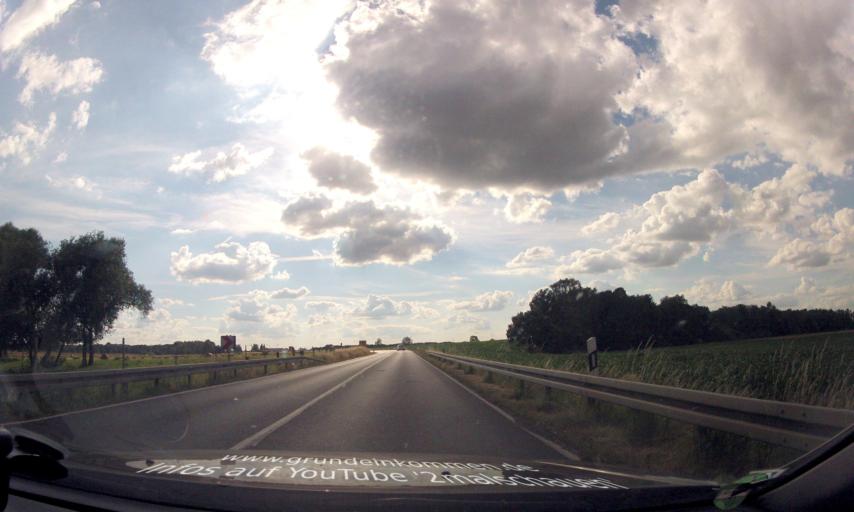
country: DE
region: Saxony
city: Bennewitz
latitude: 51.3612
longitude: 12.6826
